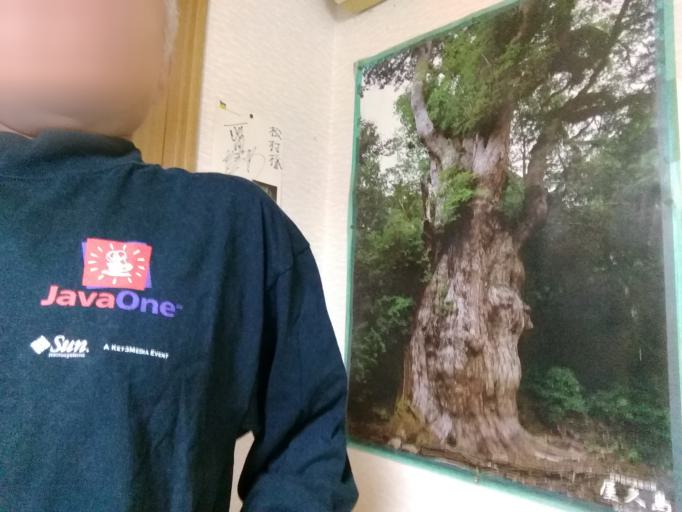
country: JP
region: Kagoshima
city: Nishinoomote
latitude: 30.2579
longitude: 130.6001
